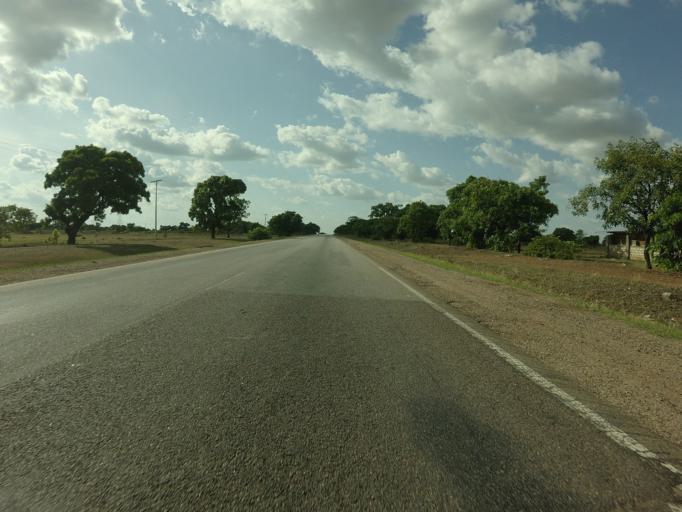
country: GH
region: Upper East
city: Bolgatanga
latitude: 10.6611
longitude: -0.8594
